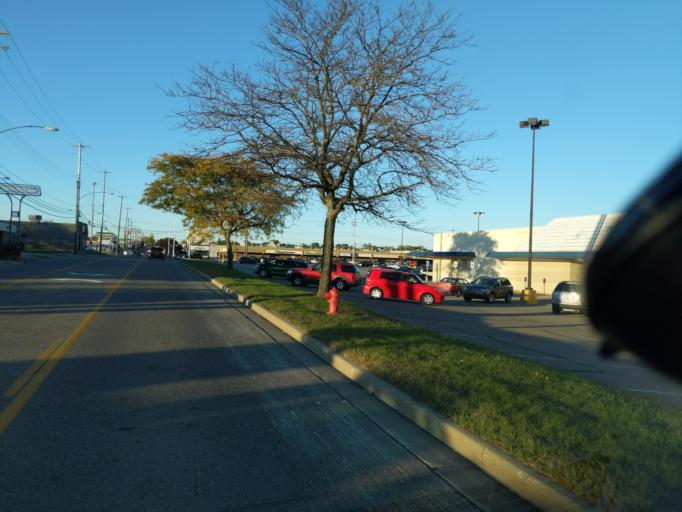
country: US
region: Michigan
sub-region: Ingham County
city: East Lansing
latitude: 42.7347
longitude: -84.5083
